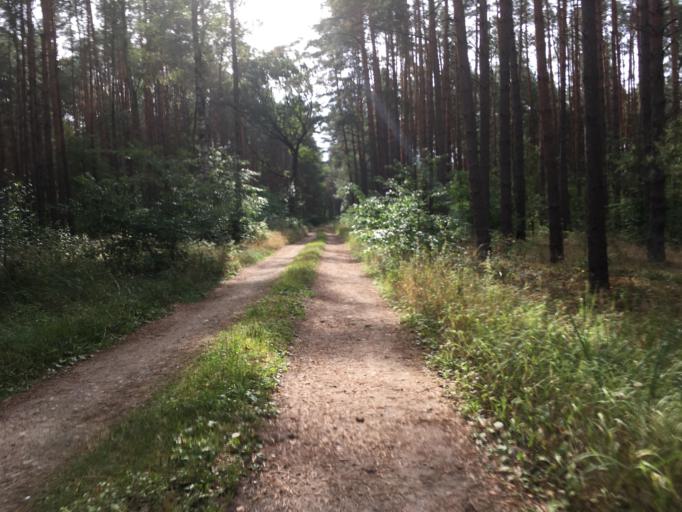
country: DE
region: Brandenburg
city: Templin
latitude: 52.9967
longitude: 13.5330
